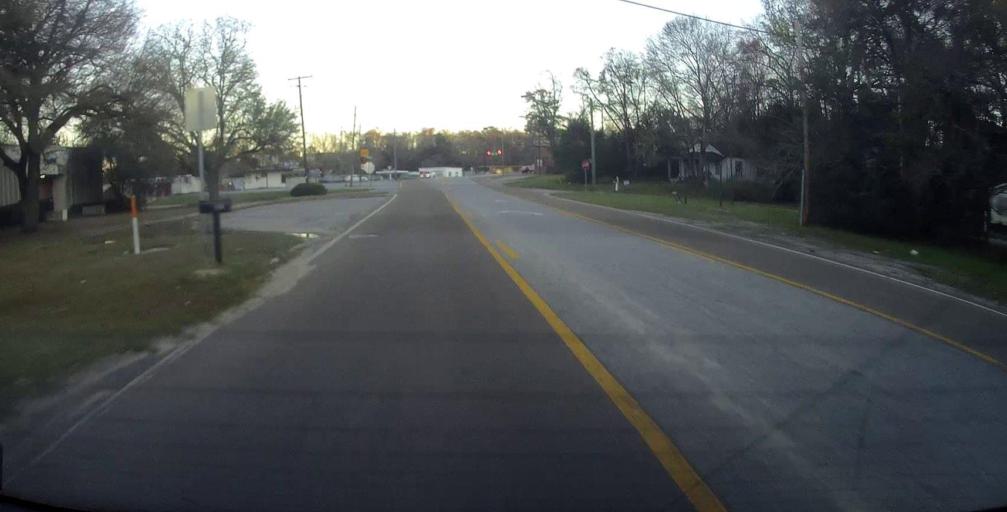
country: US
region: Alabama
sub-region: Russell County
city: Phenix City
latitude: 32.4760
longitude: -85.0249
